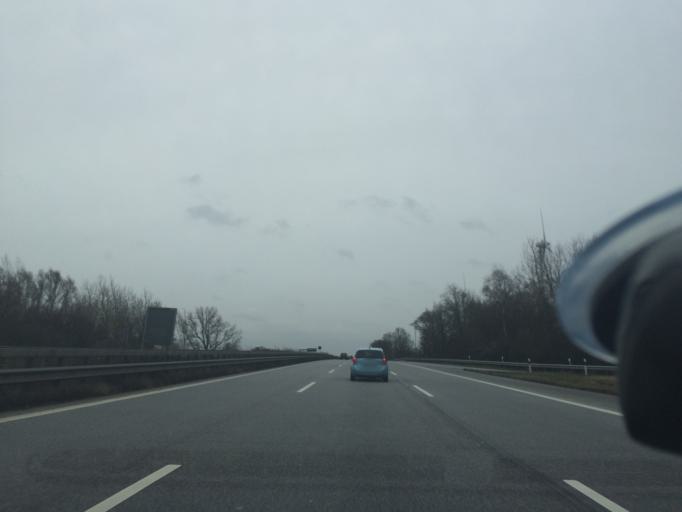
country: DE
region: Hamburg
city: Harburg
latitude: 53.4645
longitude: 10.0251
